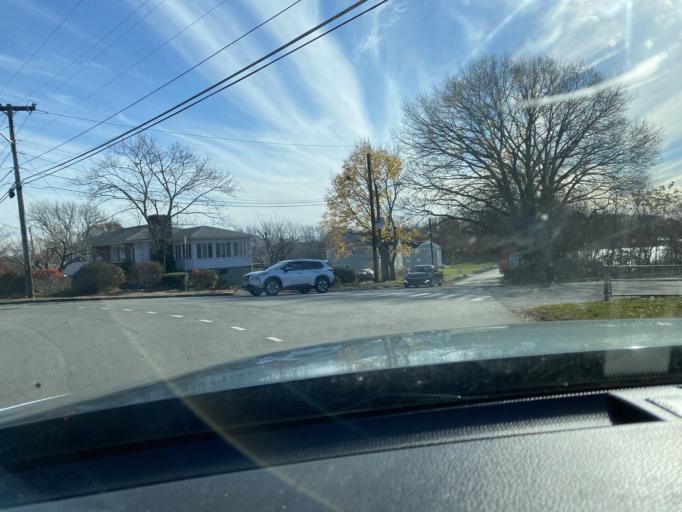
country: US
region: Massachusetts
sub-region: Norfolk County
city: Westwood
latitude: 42.1835
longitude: -71.2336
